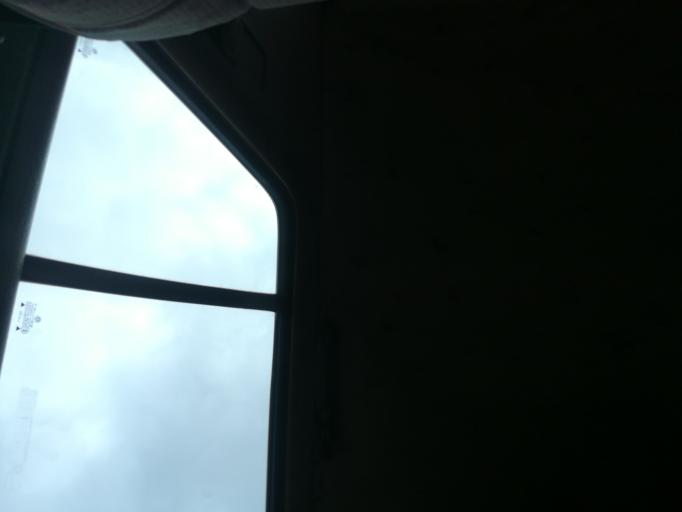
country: NG
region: Lagos
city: Ikeja
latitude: 6.5889
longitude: 3.3457
